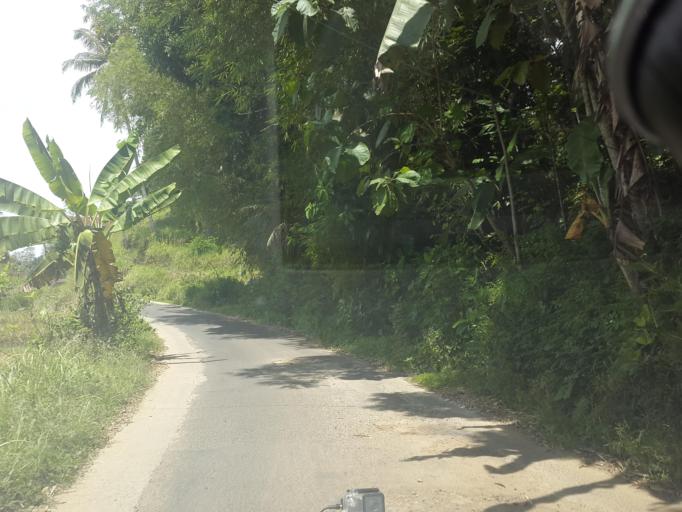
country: ID
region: Central Java
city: Sangkalputung
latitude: -7.4111
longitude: 109.0561
